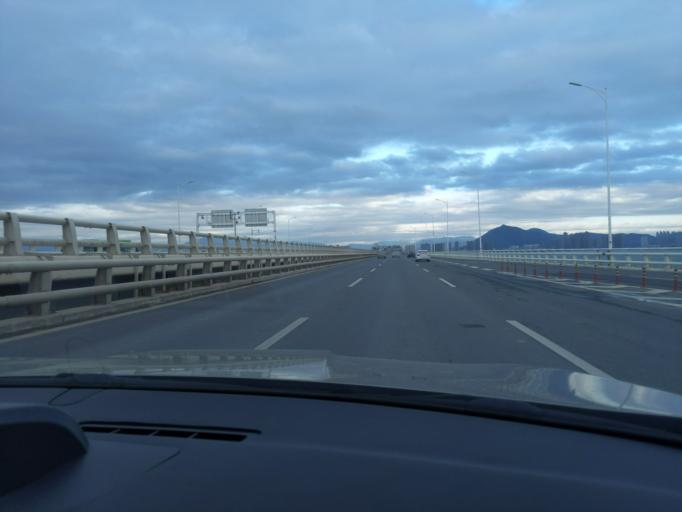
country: CN
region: Fujian
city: Yingcun
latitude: 24.5611
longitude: 118.1357
